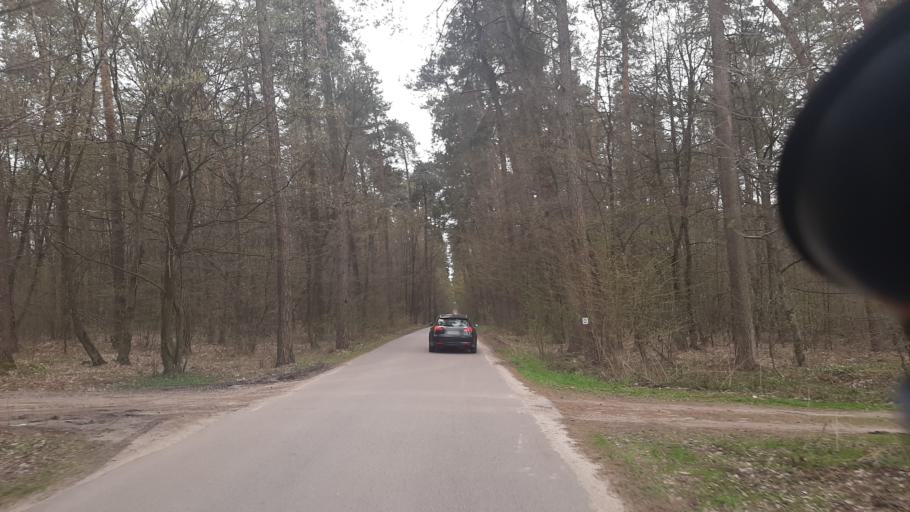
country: PL
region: Lublin Voivodeship
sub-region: Powiat lubelski
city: Niemce
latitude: 51.3742
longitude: 22.5526
